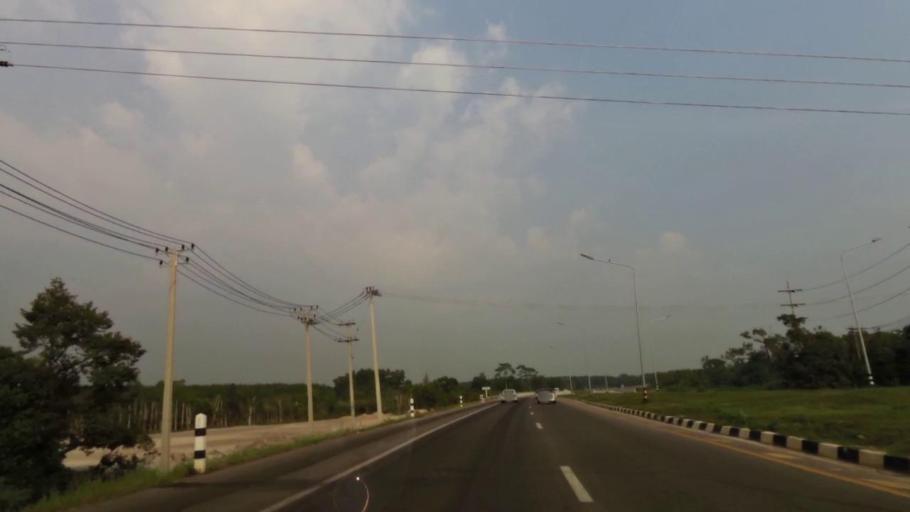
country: TH
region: Rayong
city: Klaeng
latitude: 12.8085
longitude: 101.6411
